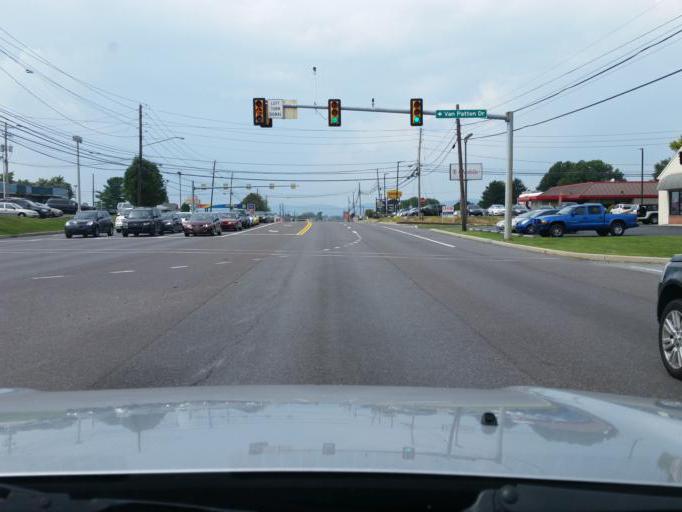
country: US
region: Pennsylvania
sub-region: Cumberland County
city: Shiremanstown
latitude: 40.2399
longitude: -76.9828
